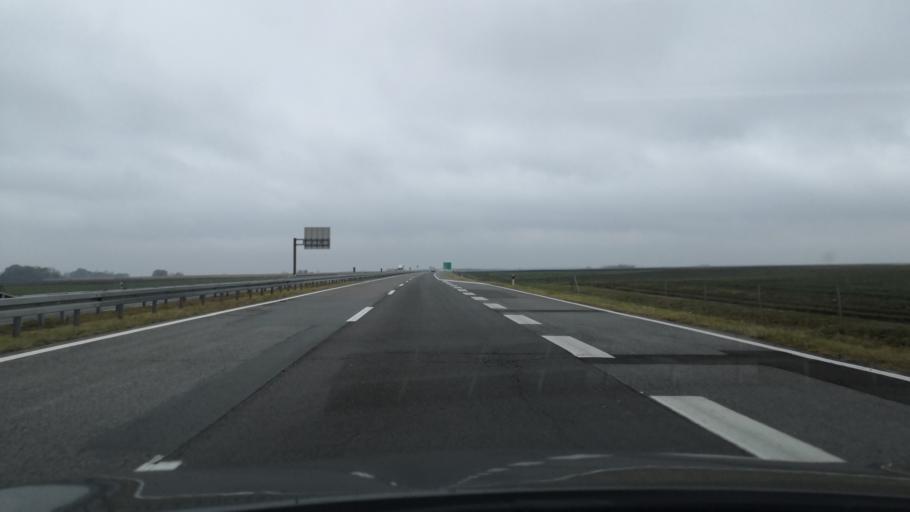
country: RS
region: Autonomna Pokrajina Vojvodina
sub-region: Severnobacki Okrug
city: Backa Topola
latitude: 45.9332
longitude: 19.7089
